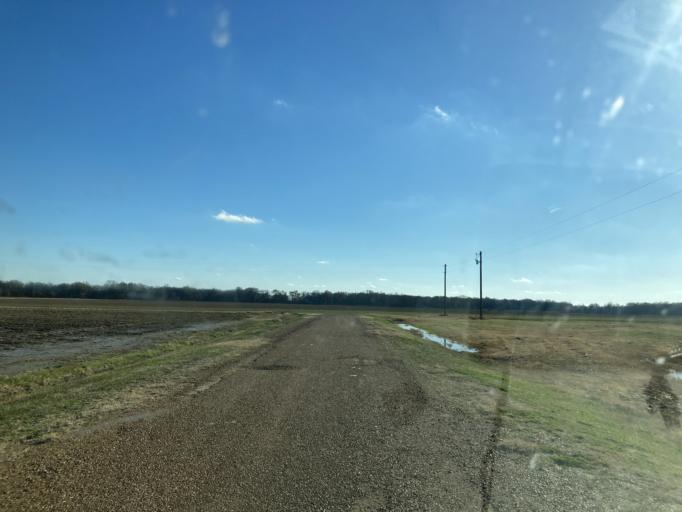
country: US
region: Mississippi
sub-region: Yazoo County
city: Yazoo City
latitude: 32.9241
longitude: -90.5058
